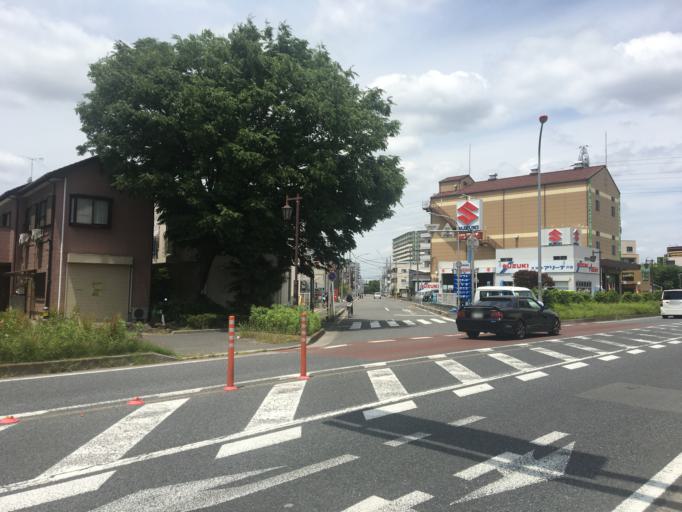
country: JP
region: Saitama
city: Shimotoda
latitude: 35.8172
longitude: 139.6819
